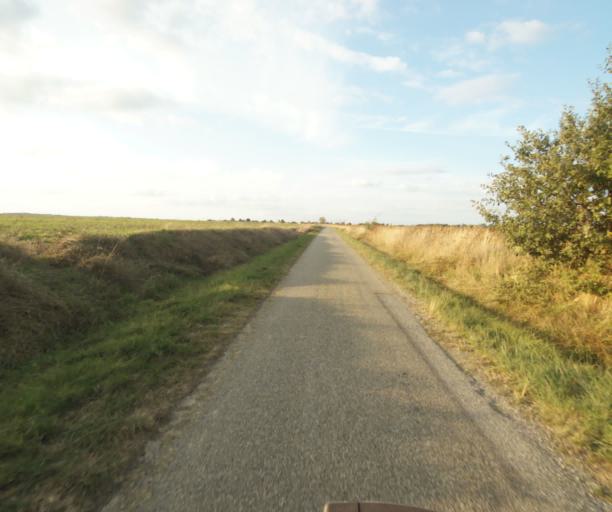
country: FR
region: Midi-Pyrenees
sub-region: Departement de la Haute-Garonne
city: Launac
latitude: 43.8138
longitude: 1.1631
